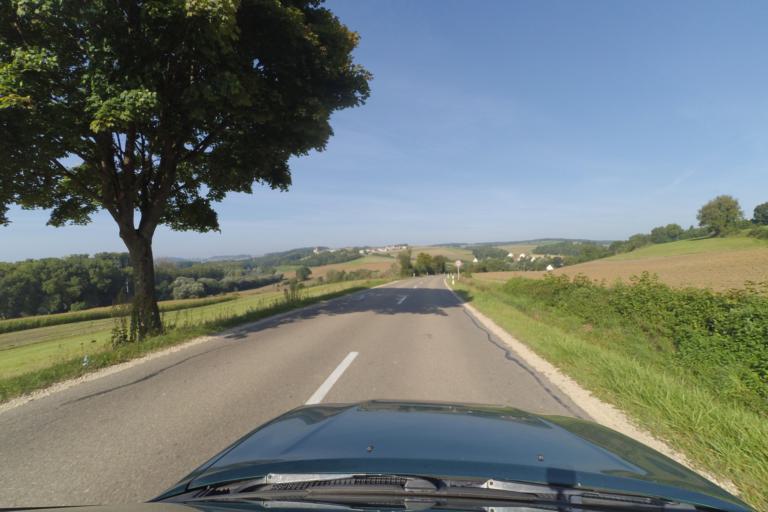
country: DE
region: Bavaria
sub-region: Swabia
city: Niederschonenfeld
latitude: 48.7433
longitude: 10.9039
